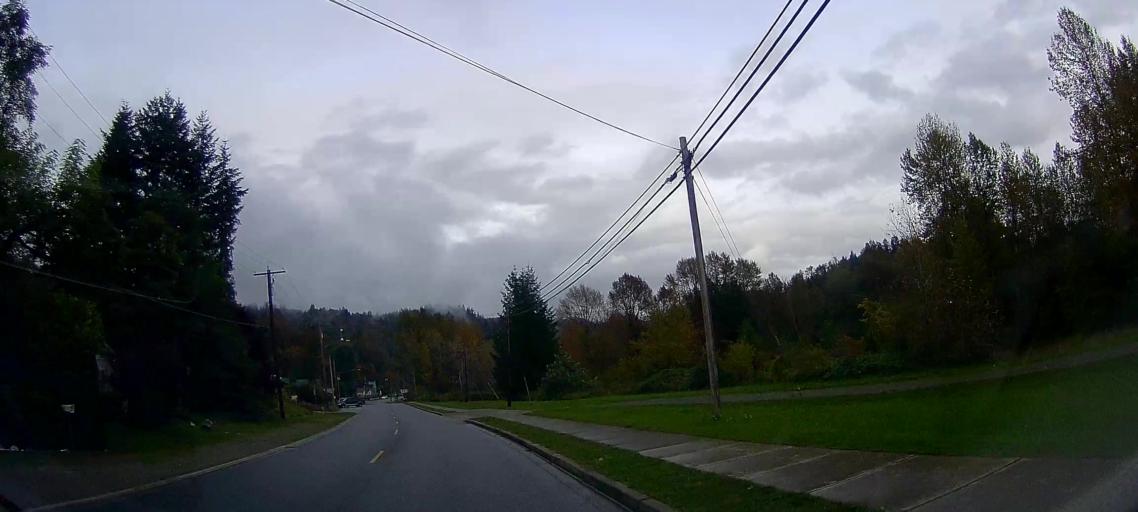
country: US
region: Washington
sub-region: Snohomish County
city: Darrington
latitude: 48.5383
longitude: -121.7558
